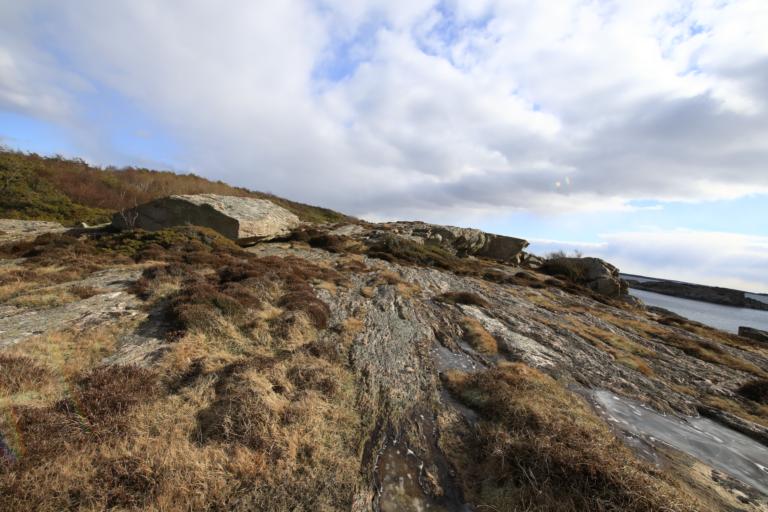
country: SE
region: Halland
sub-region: Kungsbacka Kommun
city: Frillesas
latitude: 57.2169
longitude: 12.1356
